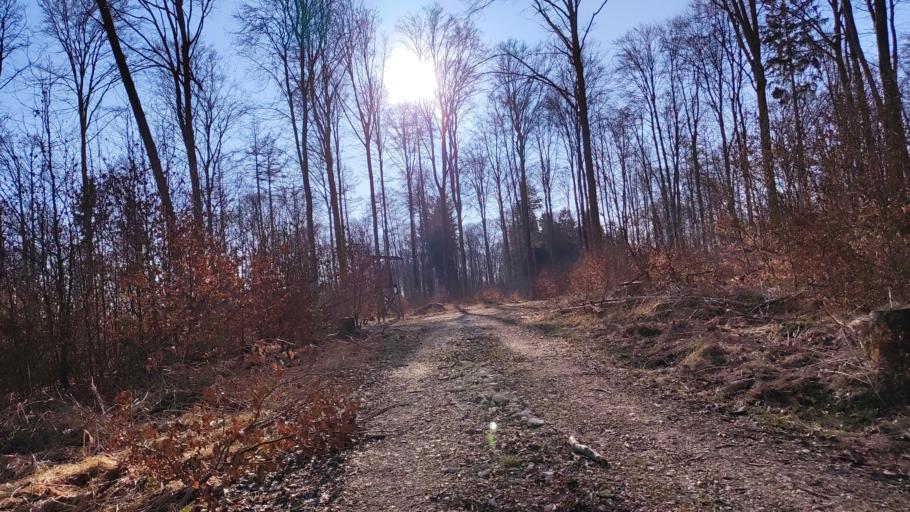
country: DE
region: Bavaria
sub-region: Swabia
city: Zusmarshausen
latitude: 48.4269
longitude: 10.6115
